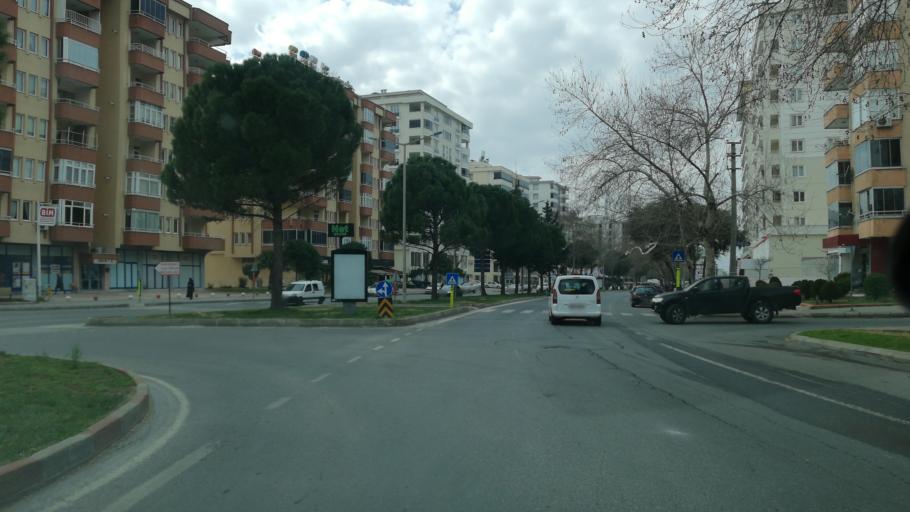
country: TR
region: Kahramanmaras
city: Kahramanmaras
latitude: 37.5848
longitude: 36.8967
